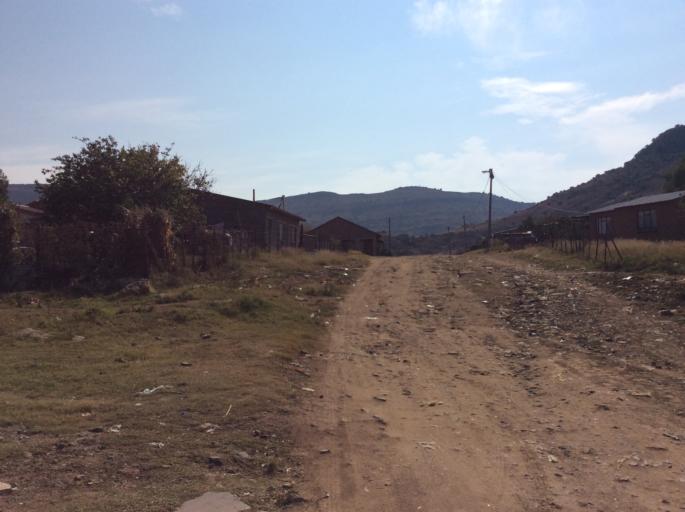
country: LS
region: Mafeteng
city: Mafeteng
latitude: -29.7208
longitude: 27.0353
